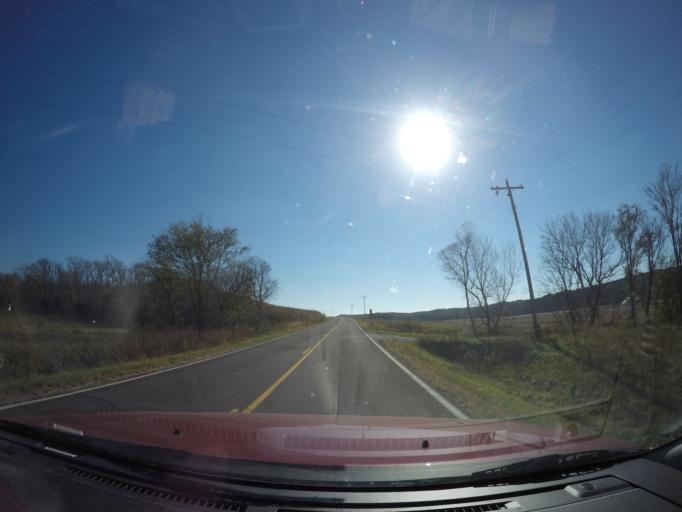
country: US
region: Kansas
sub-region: Geary County
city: Grandview Plaza
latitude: 38.9902
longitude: -96.7274
